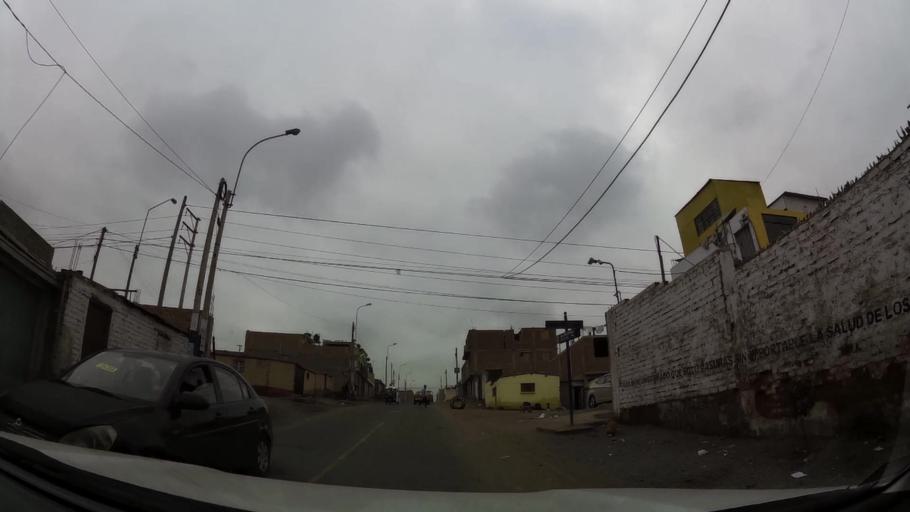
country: PE
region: Lima
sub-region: Lima
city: Surco
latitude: -12.1981
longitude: -76.9864
